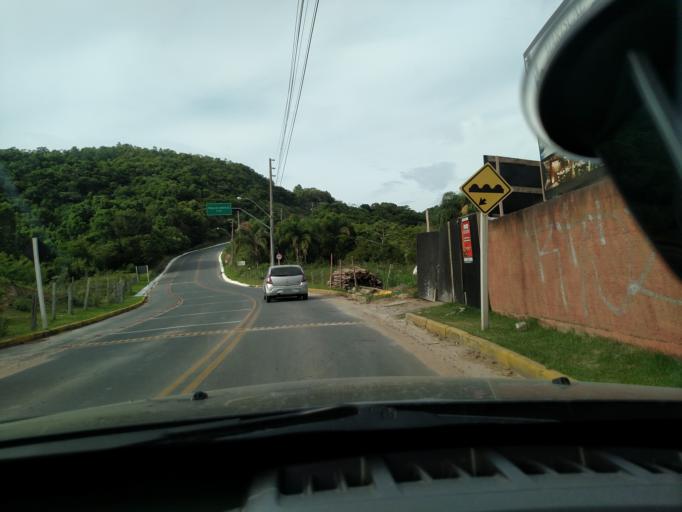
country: BR
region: Santa Catarina
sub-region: Porto Belo
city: Porto Belo
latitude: -27.1564
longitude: -48.4903
